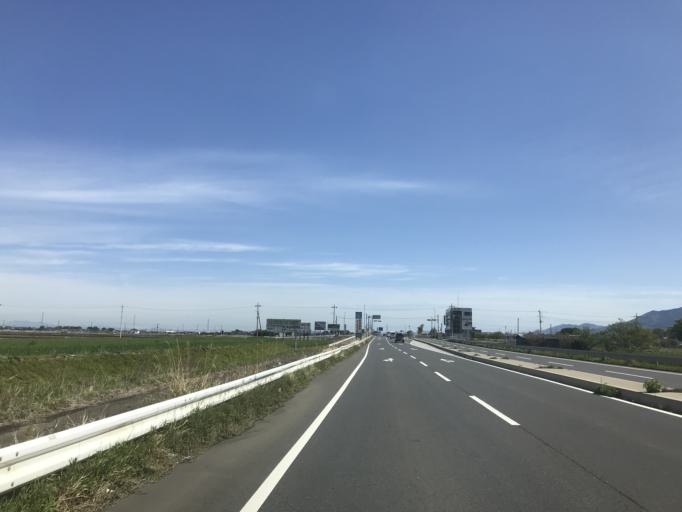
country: JP
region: Ibaraki
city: Ishige
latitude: 36.1463
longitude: 139.9901
